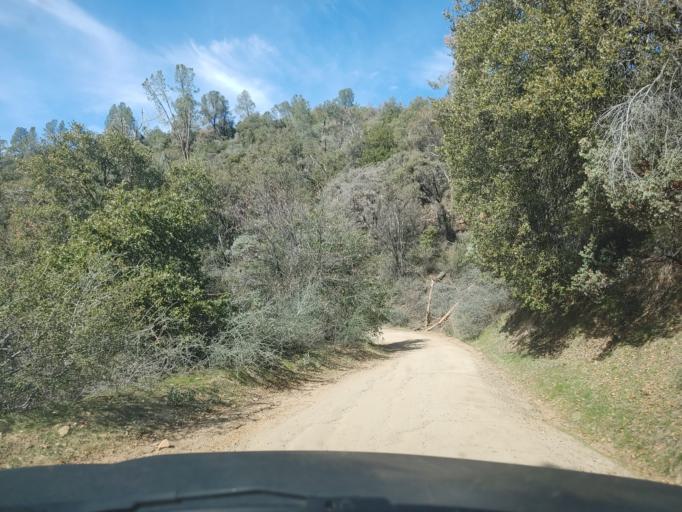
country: US
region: California
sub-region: Madera County
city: Ahwahnee
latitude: 37.4159
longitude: -119.6939
